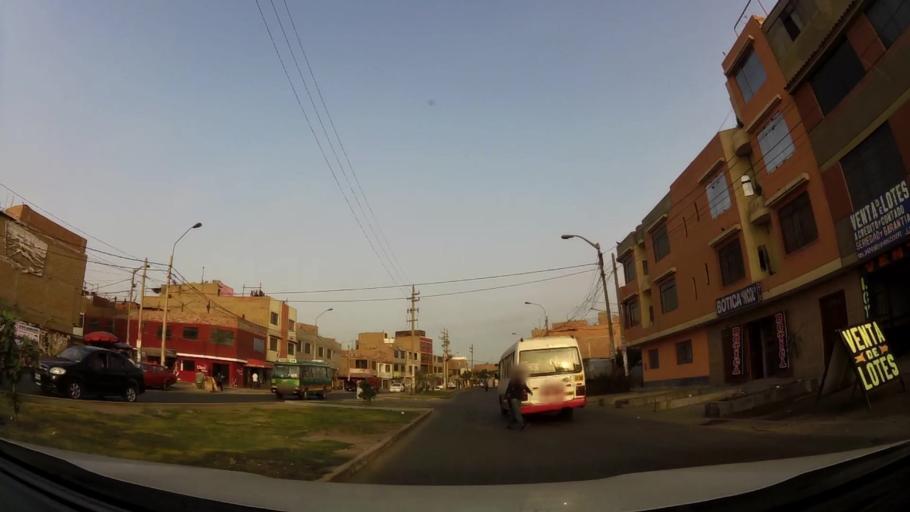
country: PE
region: Callao
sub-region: Callao
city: Callao
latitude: -11.9945
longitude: -77.1100
